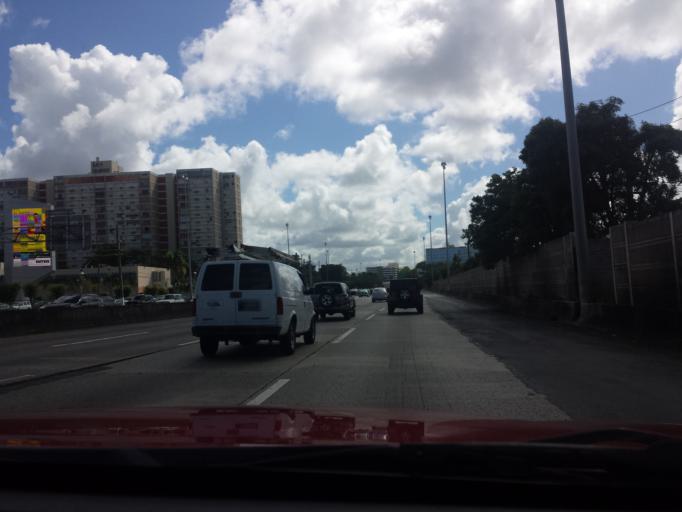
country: PR
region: Catano
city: Catano
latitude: 18.4051
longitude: -66.0702
